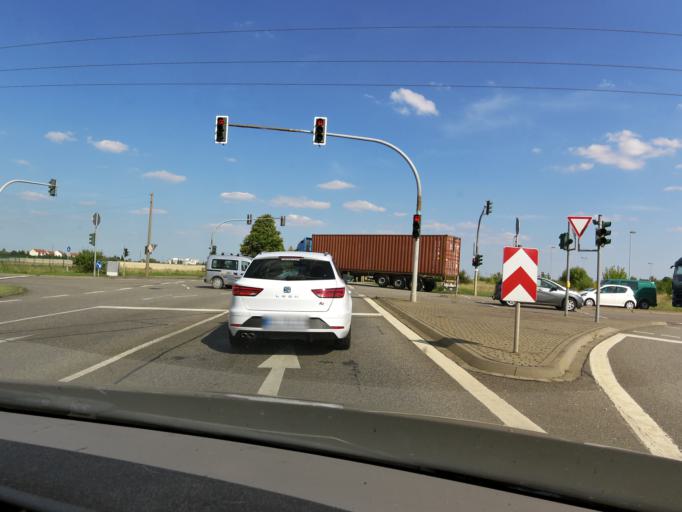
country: DE
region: Saxony-Anhalt
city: Dieskau
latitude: 51.4422
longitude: 12.0432
